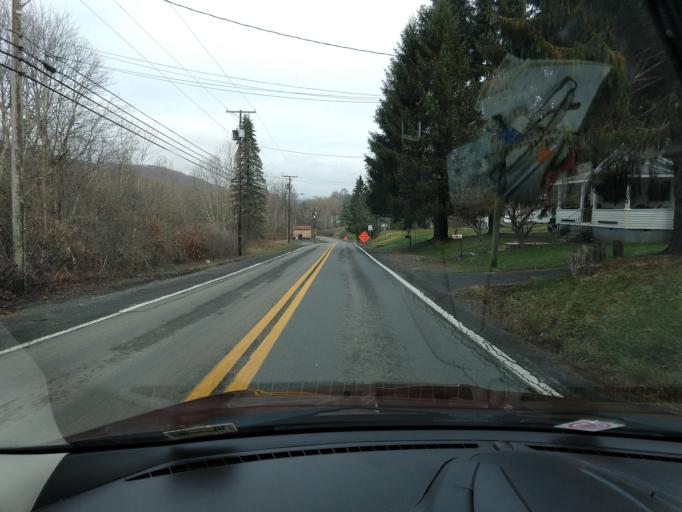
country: US
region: West Virginia
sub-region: Greenbrier County
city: Rainelle
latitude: 38.0603
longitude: -80.7081
